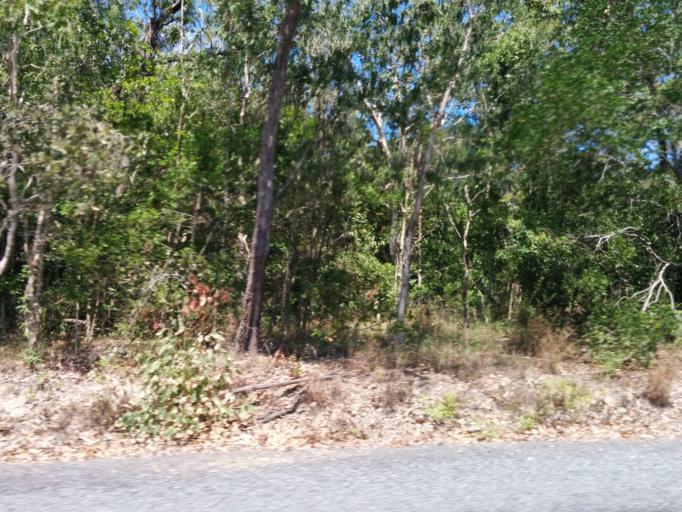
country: AU
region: Queensland
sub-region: Cairns
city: Palm Cove
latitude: -16.6810
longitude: 145.5745
